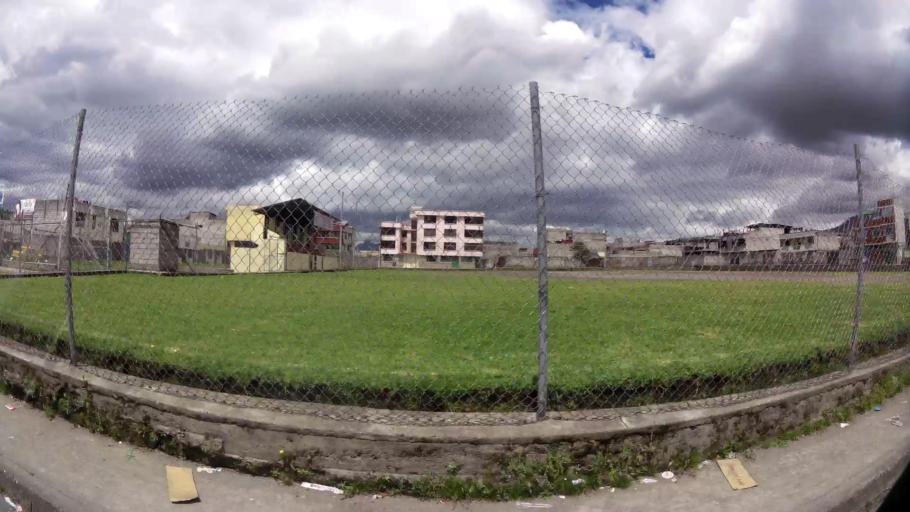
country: EC
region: Pichincha
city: Sangolqui
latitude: -0.3355
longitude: -78.5401
